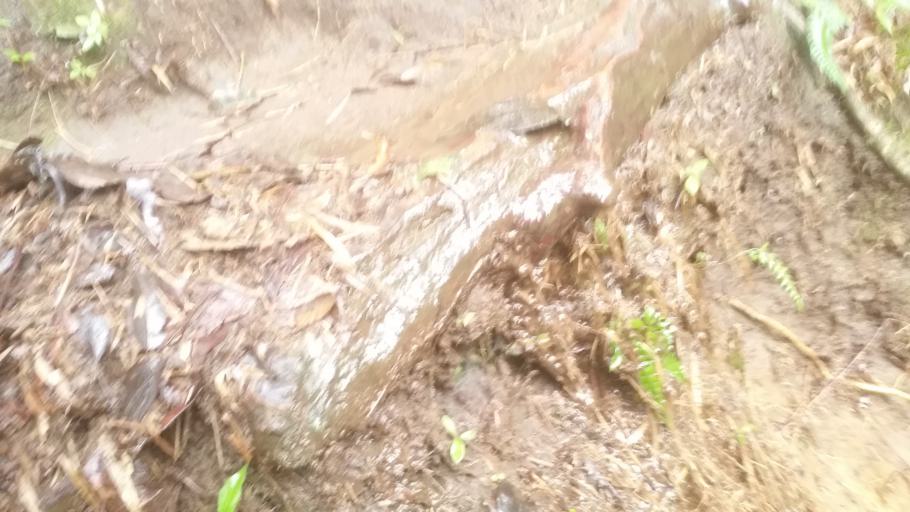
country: CO
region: Quindio
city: Calarca
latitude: 4.4810
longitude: -75.6297
